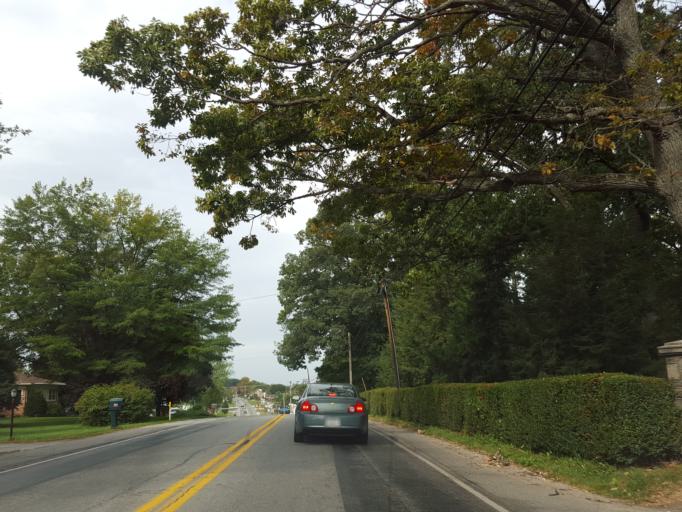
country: US
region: Pennsylvania
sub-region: York County
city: Spry
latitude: 39.9070
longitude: -76.6682
